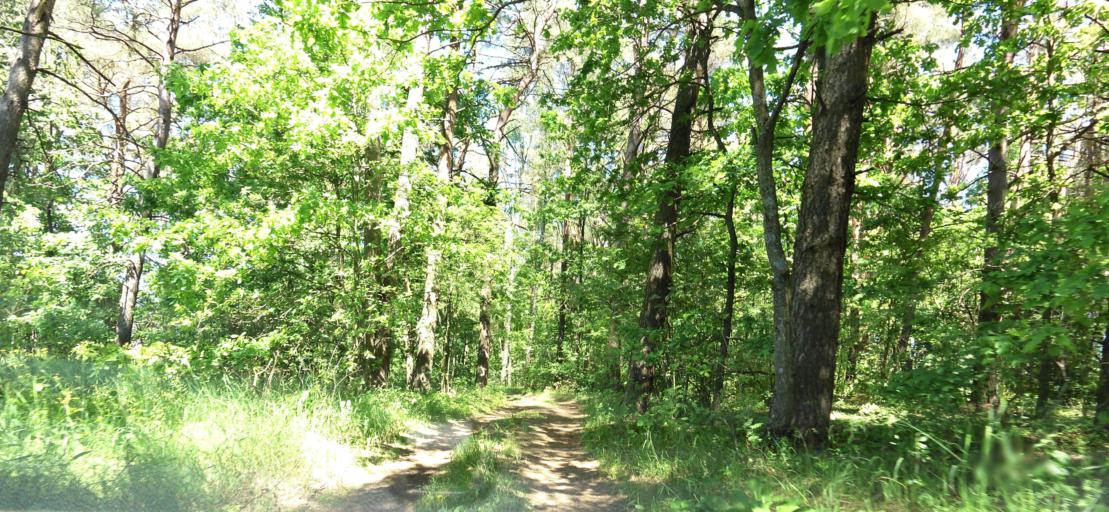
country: LT
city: Moletai
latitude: 55.0739
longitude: 25.2400
